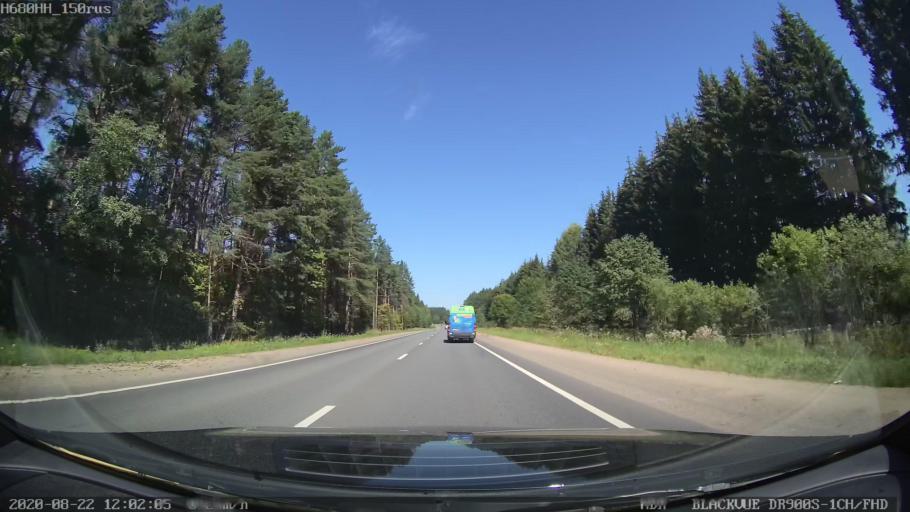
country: RU
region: Tverskaya
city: Rameshki
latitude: 57.2379
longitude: 36.1001
